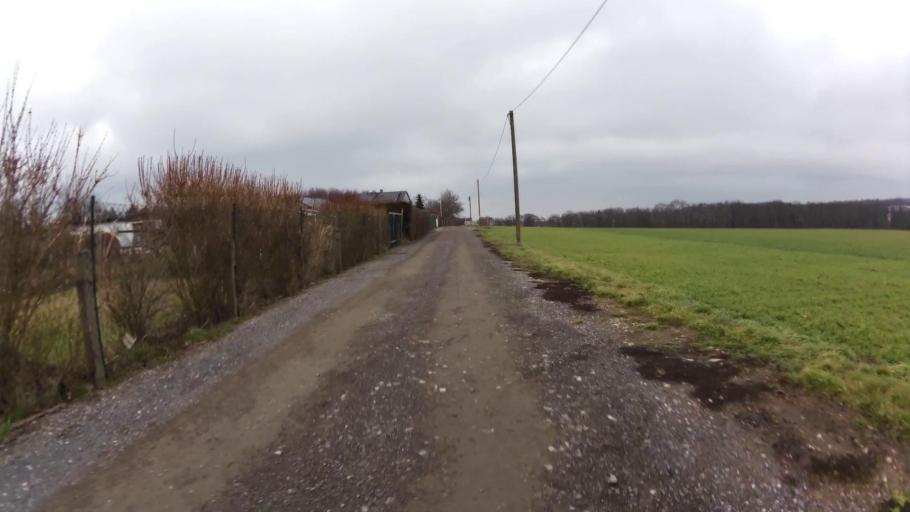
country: DE
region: Thuringia
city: Weimar
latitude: 50.9666
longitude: 11.3161
